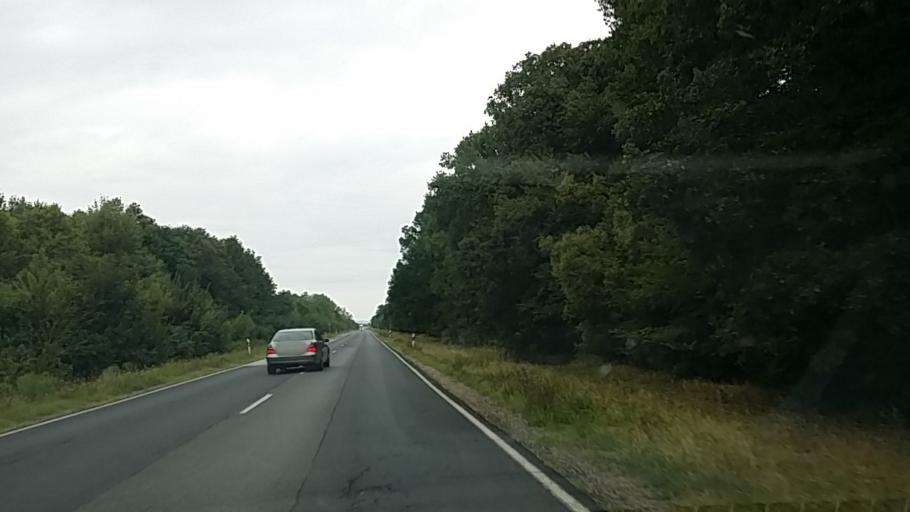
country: HU
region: Gyor-Moson-Sopron
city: Kapuvar
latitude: 47.5877
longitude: 16.9709
